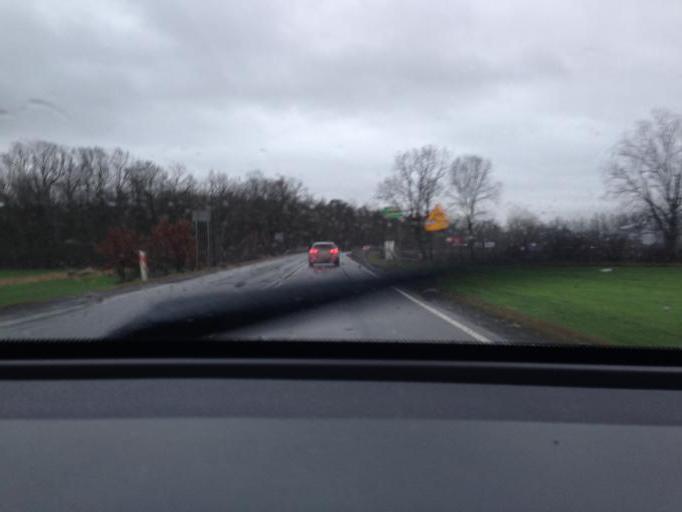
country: PL
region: Opole Voivodeship
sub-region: Powiat opolski
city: Wegry
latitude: 50.7080
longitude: 17.9852
